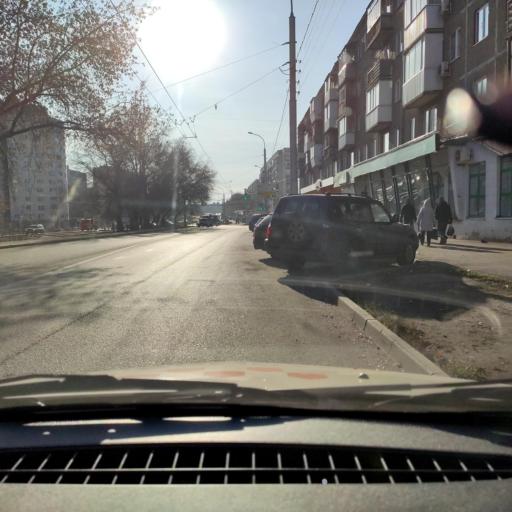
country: RU
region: Bashkortostan
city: Ufa
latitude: 54.8140
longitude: 56.1267
